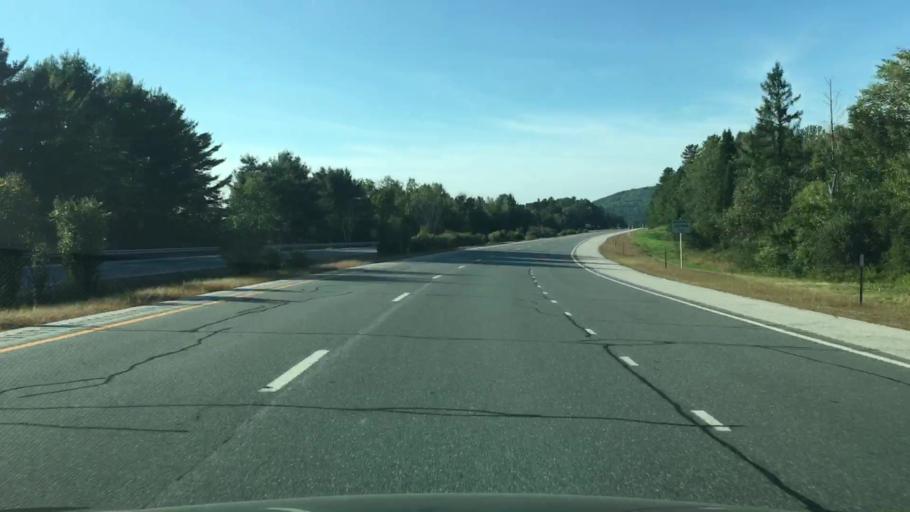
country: US
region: New Hampshire
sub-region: Grafton County
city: Littleton
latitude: 44.2309
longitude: -71.7516
